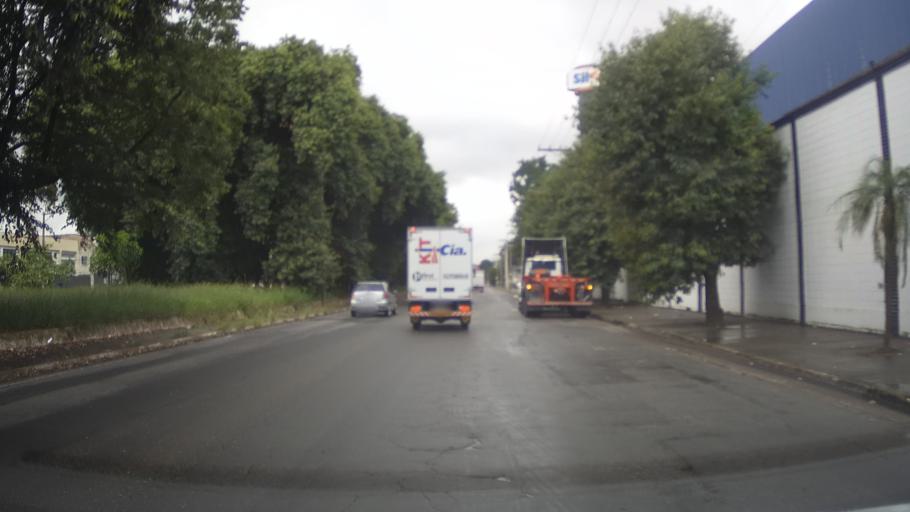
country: BR
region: Sao Paulo
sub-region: Guarulhos
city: Guarulhos
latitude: -23.4767
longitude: -46.4679
